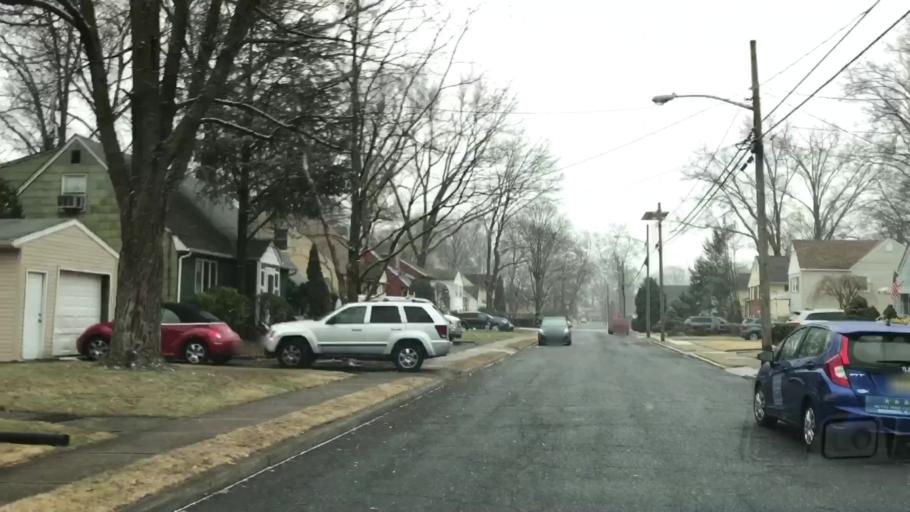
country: US
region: New Jersey
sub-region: Bergen County
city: New Milford
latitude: 40.9310
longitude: -74.0103
